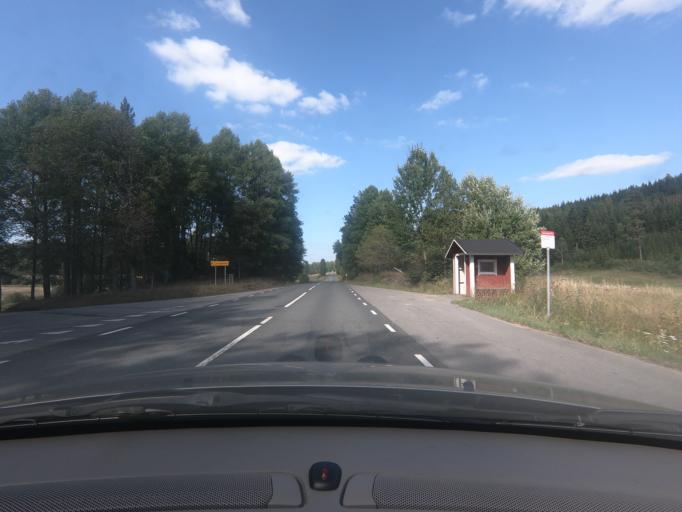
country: SE
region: Joenkoeping
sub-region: Vetlanda Kommun
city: Landsbro
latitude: 57.3358
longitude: 14.8700
